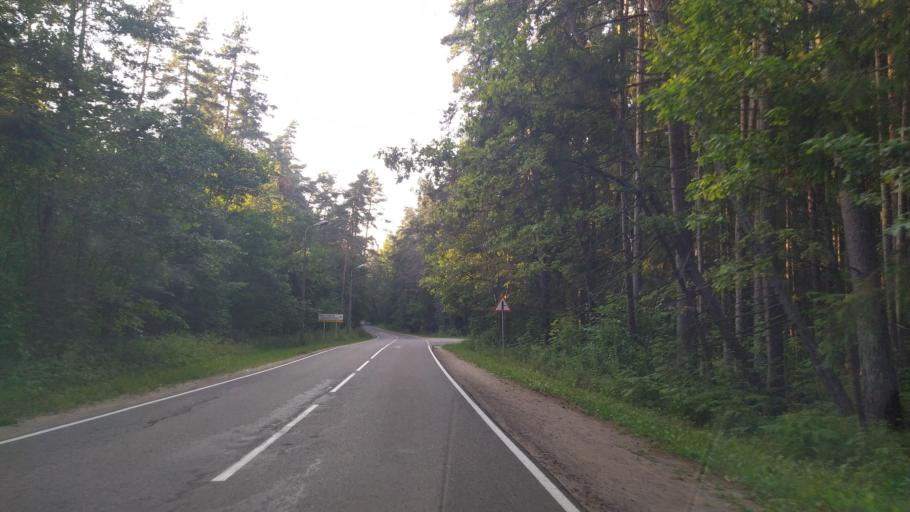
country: RU
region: Pskov
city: Pushkinskiye Gory
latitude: 57.0317
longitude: 28.9214
